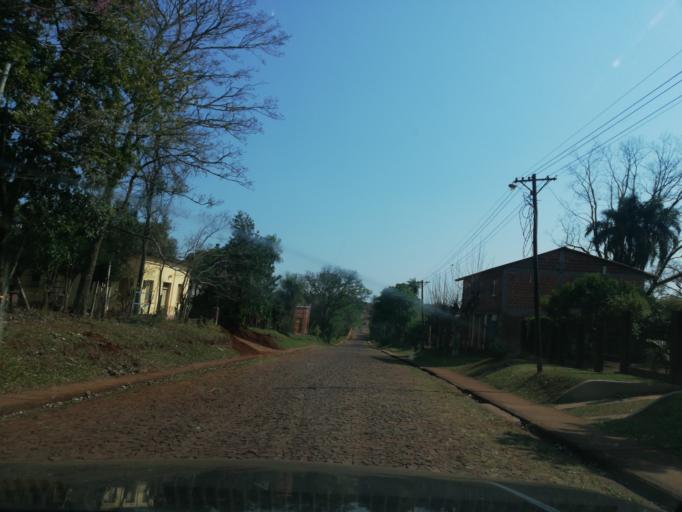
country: AR
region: Misiones
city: Bonpland
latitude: -27.4844
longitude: -55.4800
